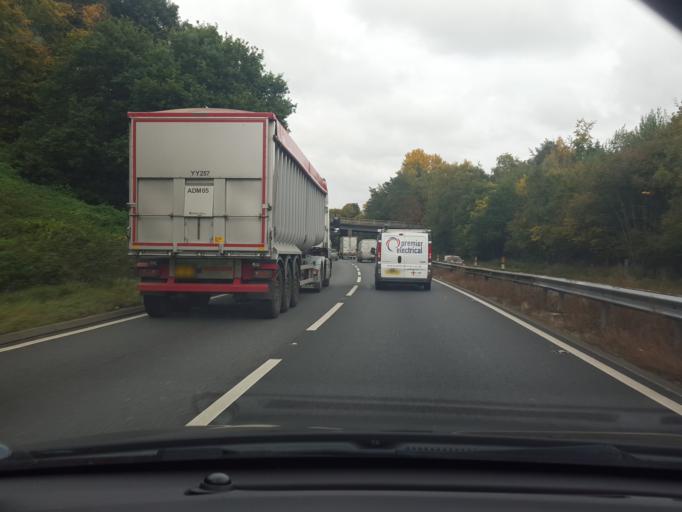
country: GB
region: England
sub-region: Suffolk
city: East Bergholt
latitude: 51.9591
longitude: 0.9709
